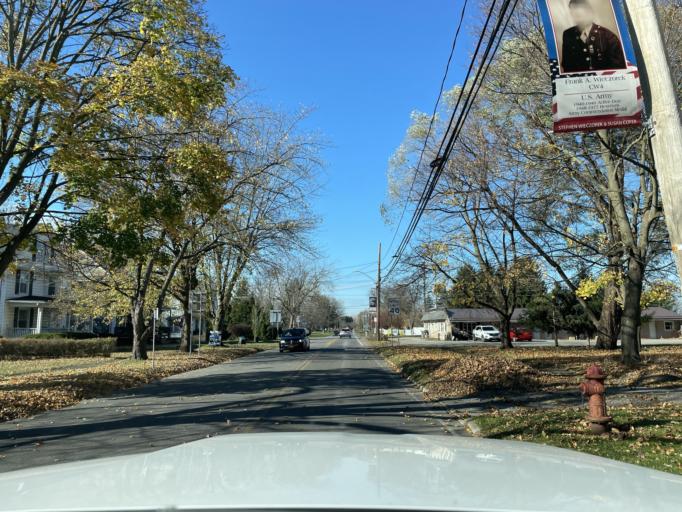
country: US
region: New York
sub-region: Orleans County
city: Medina
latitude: 43.2208
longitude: -78.4052
